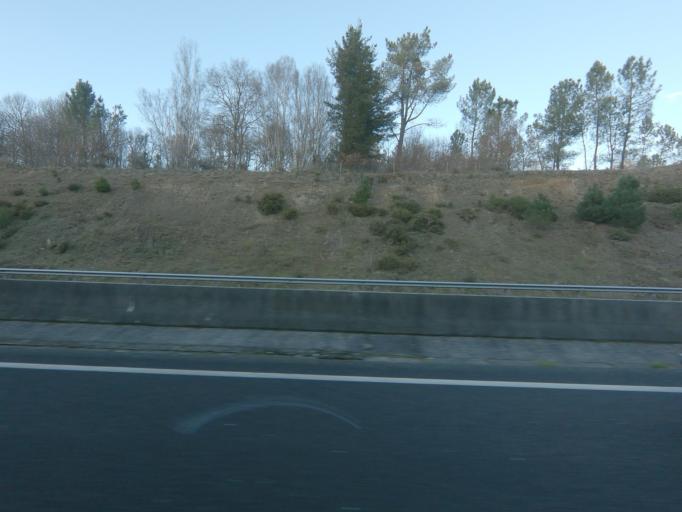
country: ES
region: Galicia
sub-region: Provincia de Pontevedra
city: Lalin
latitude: 42.6324
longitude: -8.1254
